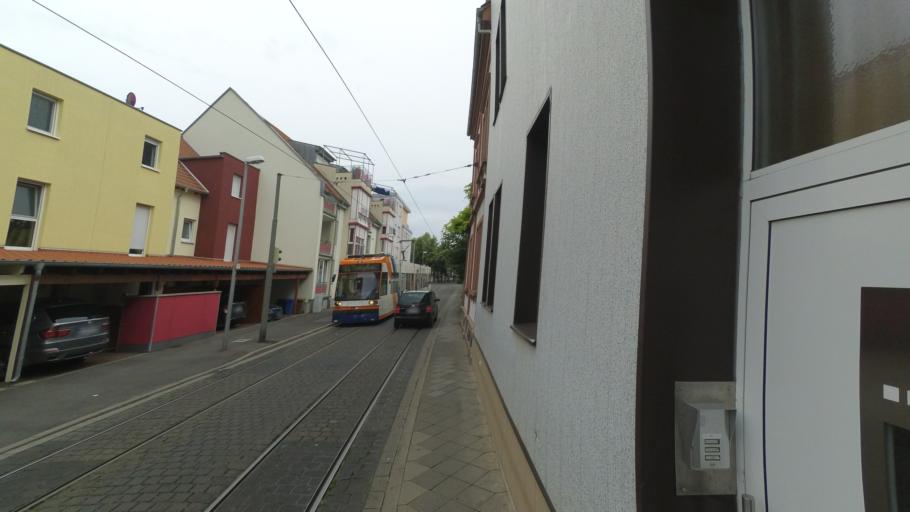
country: DE
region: Rheinland-Pfalz
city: Ludwigshafen am Rhein
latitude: 49.4973
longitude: 8.4134
